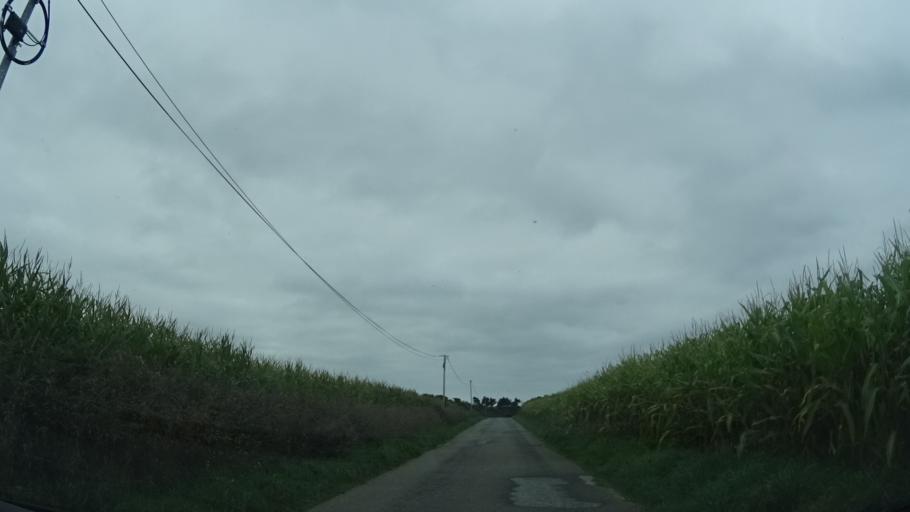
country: FR
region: Brittany
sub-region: Departement du Finistere
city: Lampaul-Plouarzel
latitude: 48.4537
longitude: -4.7566
